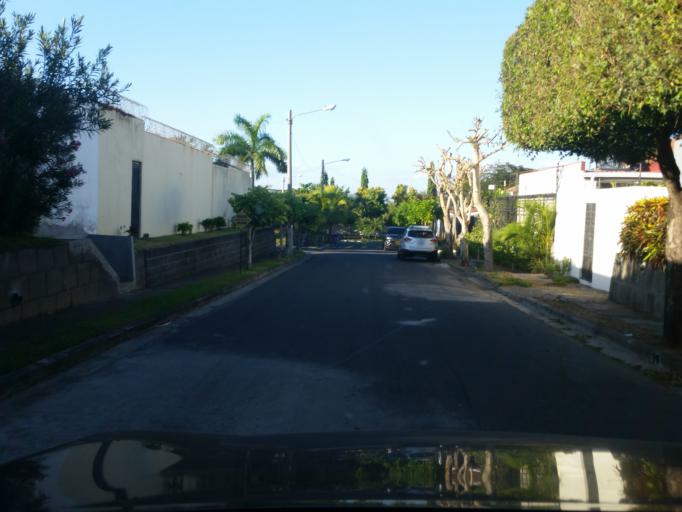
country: NI
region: Managua
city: Managua
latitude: 12.0993
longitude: -86.2553
